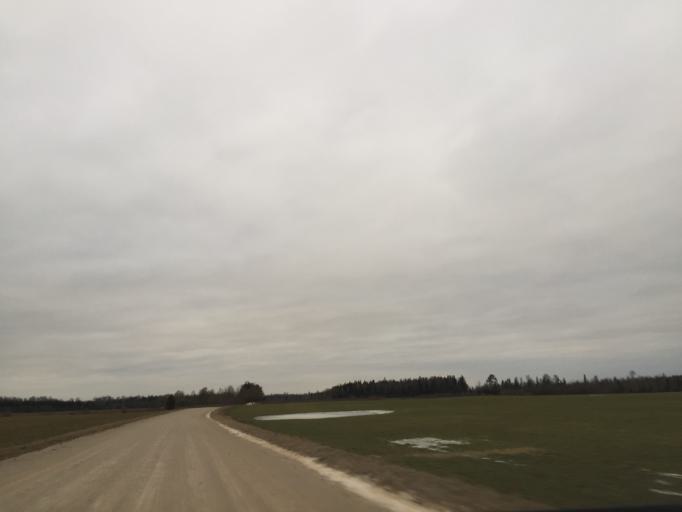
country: LT
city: Zagare
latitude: 56.2786
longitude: 23.2601
